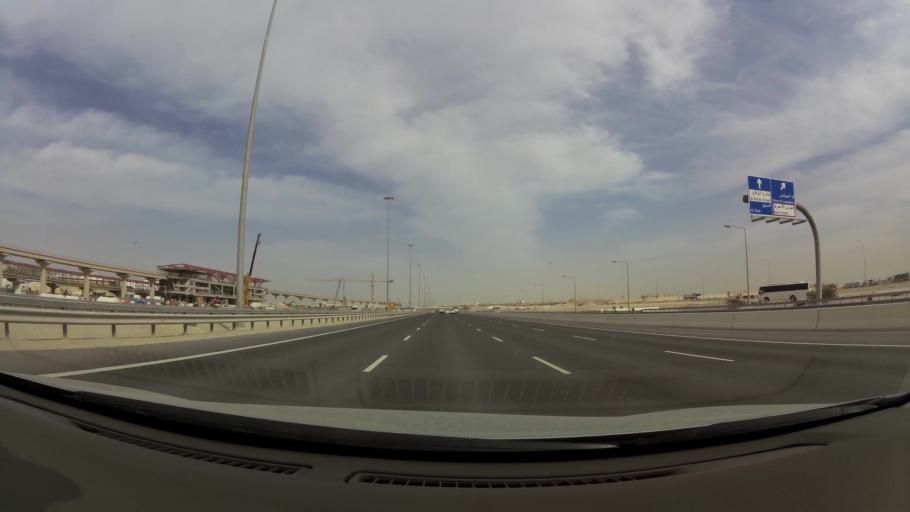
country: QA
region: Baladiyat ar Rayyan
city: Ar Rayyan
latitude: 25.3241
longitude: 51.3449
